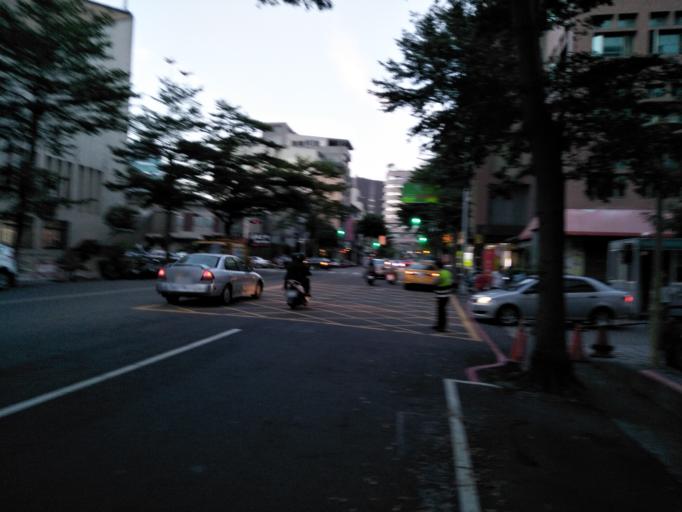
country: TW
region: Taiwan
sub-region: Taichung City
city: Taichung
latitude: 24.1514
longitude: 120.6820
